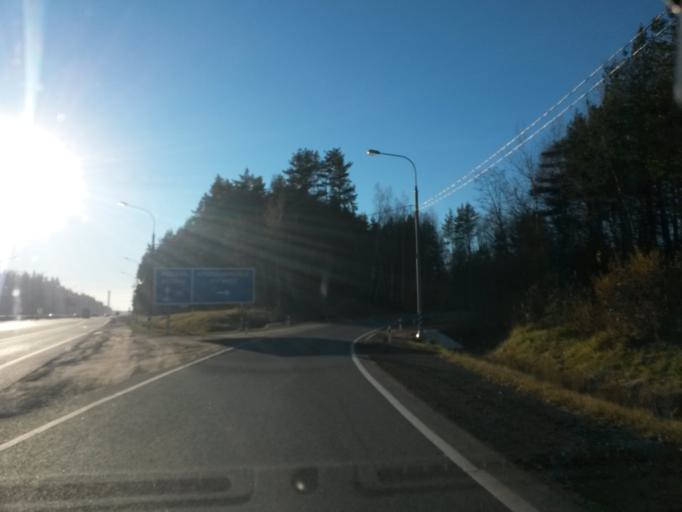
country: RU
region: Moskovskaya
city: Zelenogradskiy
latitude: 56.1052
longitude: 37.9570
